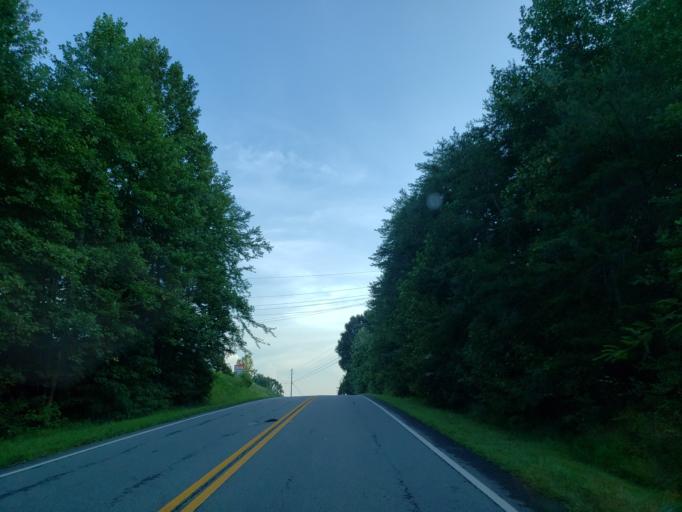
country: US
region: Georgia
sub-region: Lumpkin County
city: Dahlonega
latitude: 34.5544
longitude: -83.9689
